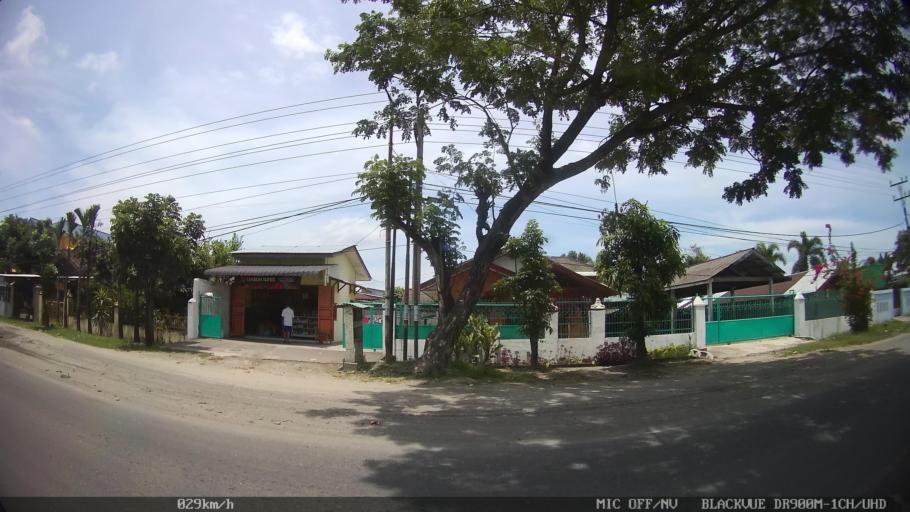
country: ID
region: North Sumatra
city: Labuhan Deli
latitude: 3.7505
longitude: 98.6756
